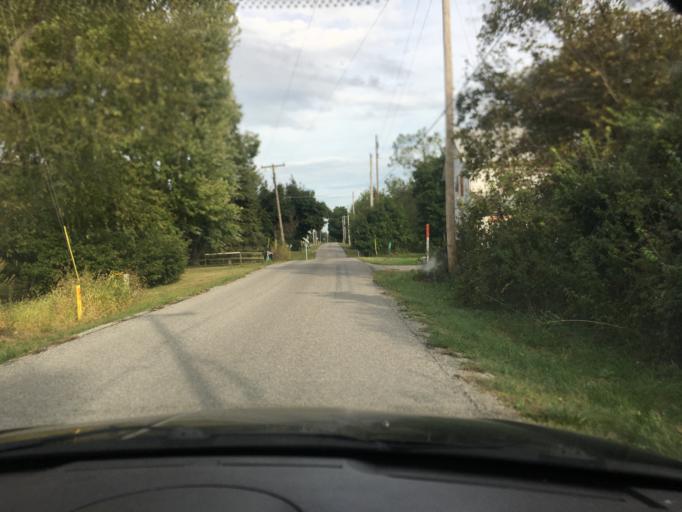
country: US
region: Ohio
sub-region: Logan County
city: Bellefontaine
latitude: 40.3180
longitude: -83.7677
